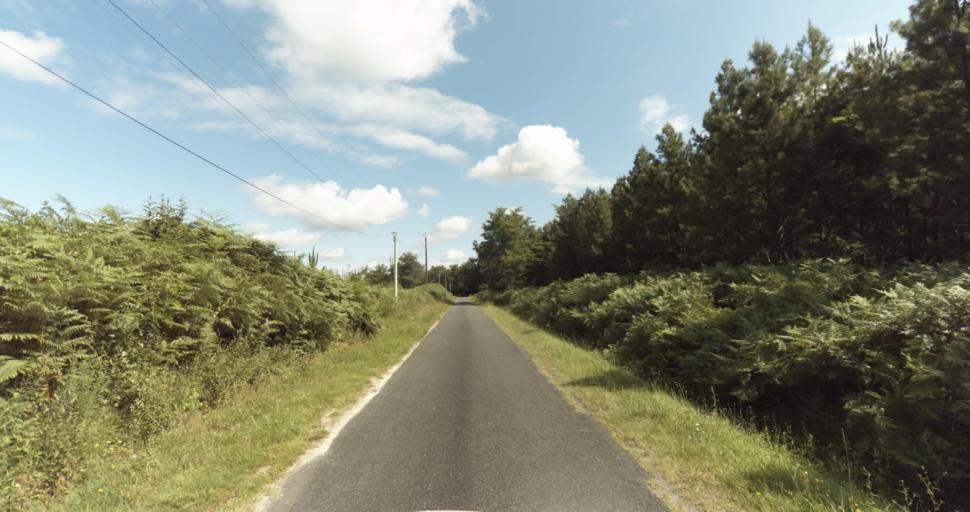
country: FR
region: Aquitaine
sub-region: Departement de la Gironde
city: Bazas
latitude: 44.4525
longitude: -0.2171
